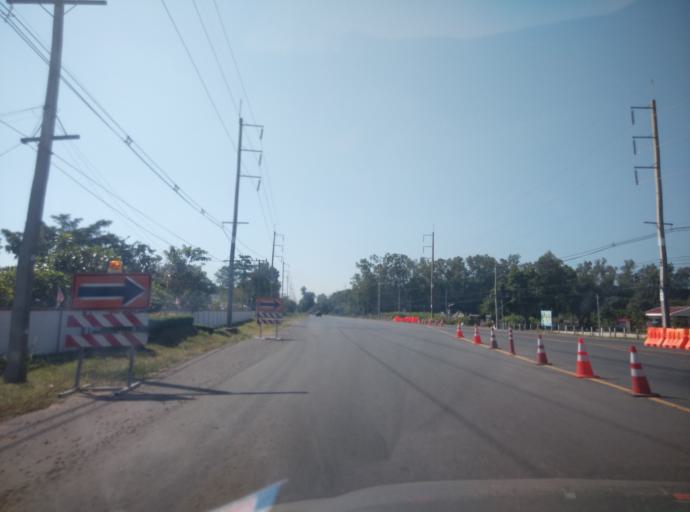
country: TH
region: Sisaket
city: Si Sa Ket
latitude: 15.1181
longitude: 104.2847
